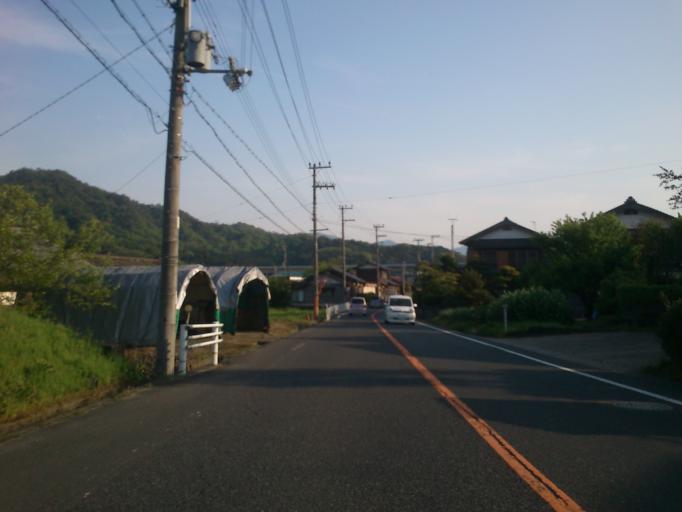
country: JP
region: Kyoto
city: Miyazu
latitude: 35.5562
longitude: 135.1392
